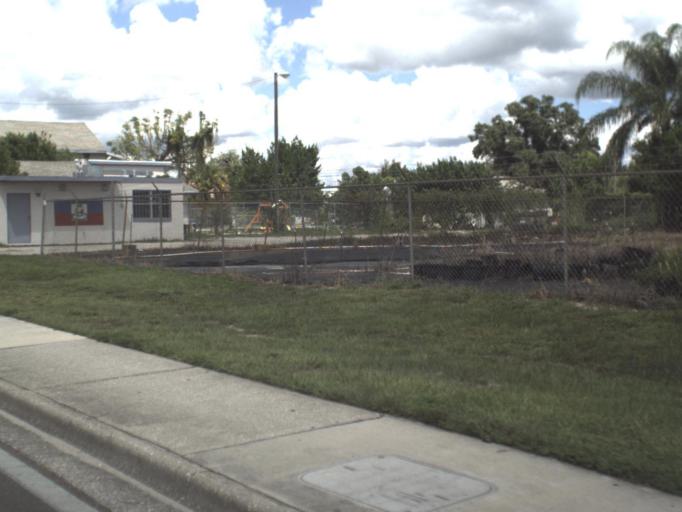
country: US
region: Florida
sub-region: Polk County
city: Winter Haven
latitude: 28.0415
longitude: -81.7267
